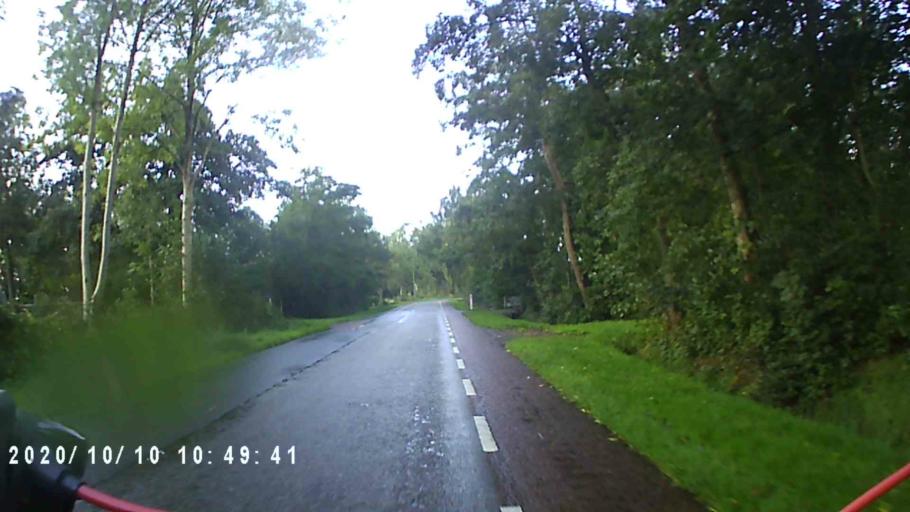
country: NL
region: Groningen
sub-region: Gemeente Grootegast
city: Grootegast
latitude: 53.1609
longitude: 6.2380
